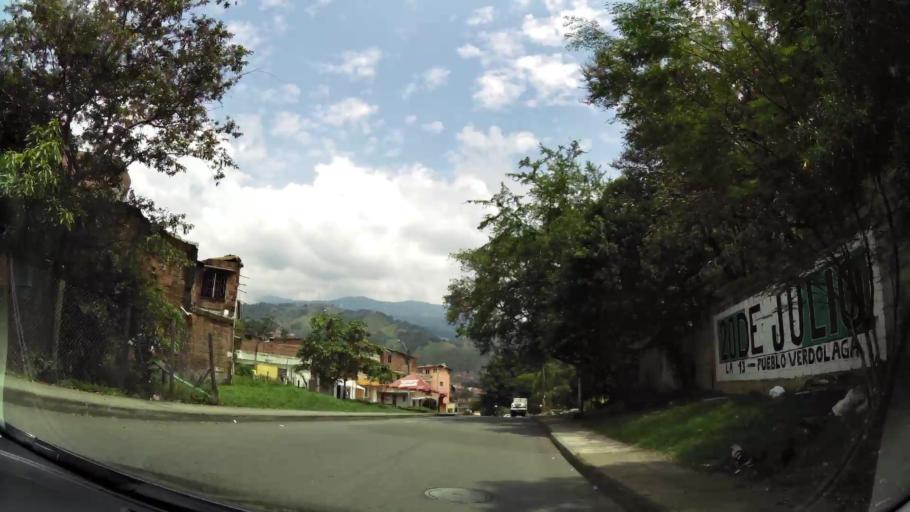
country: CO
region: Antioquia
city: Medellin
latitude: 6.2511
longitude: -75.6189
